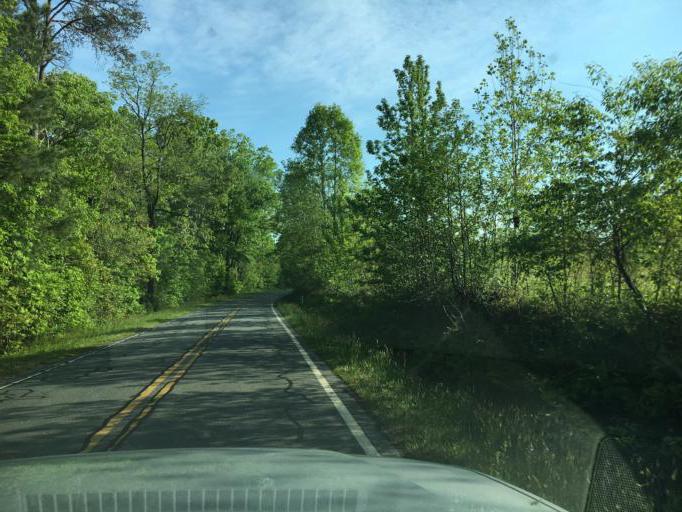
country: US
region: North Carolina
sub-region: Rutherford County
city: Rutherfordton
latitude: 35.3233
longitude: -81.9905
